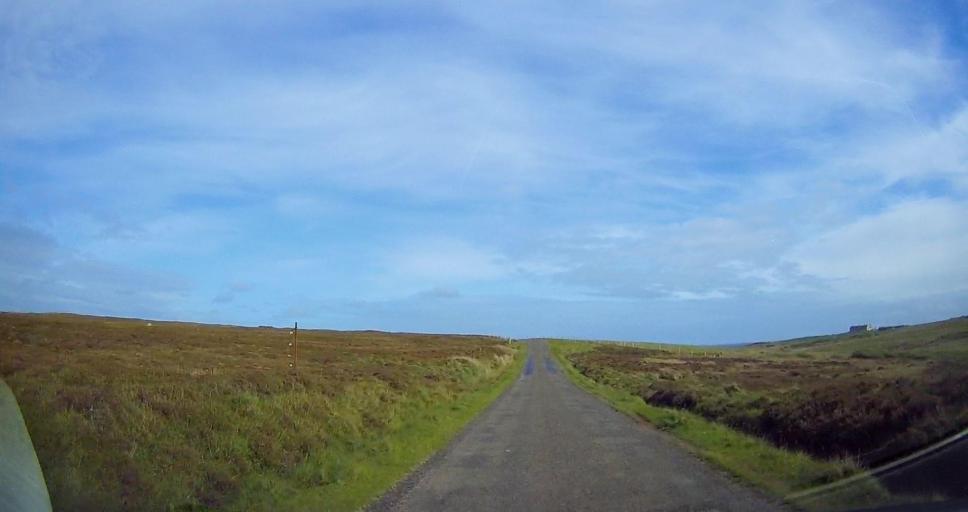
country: GB
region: Scotland
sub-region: Orkney Islands
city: Stromness
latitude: 58.8540
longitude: -3.2093
